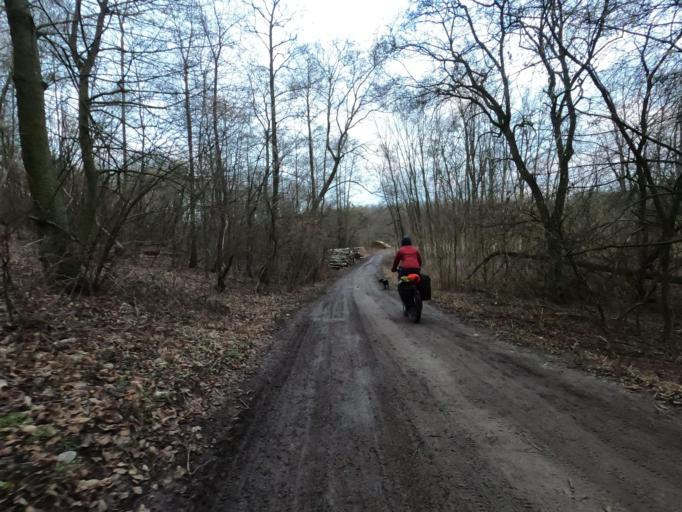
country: PL
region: Greater Poland Voivodeship
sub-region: Powiat pilski
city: Wyrzysk
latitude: 53.1164
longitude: 17.2079
